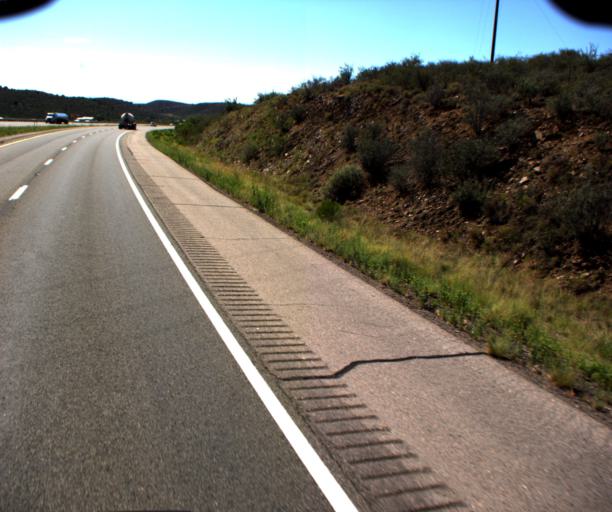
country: US
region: Arizona
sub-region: Yavapai County
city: Mayer
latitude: 34.3971
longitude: -112.2252
